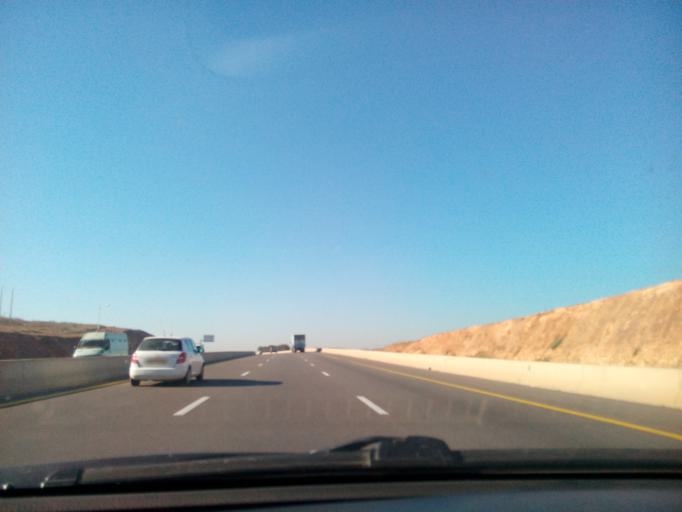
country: DZ
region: Chlef
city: Oued Sly
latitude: 36.0744
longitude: 1.1757
